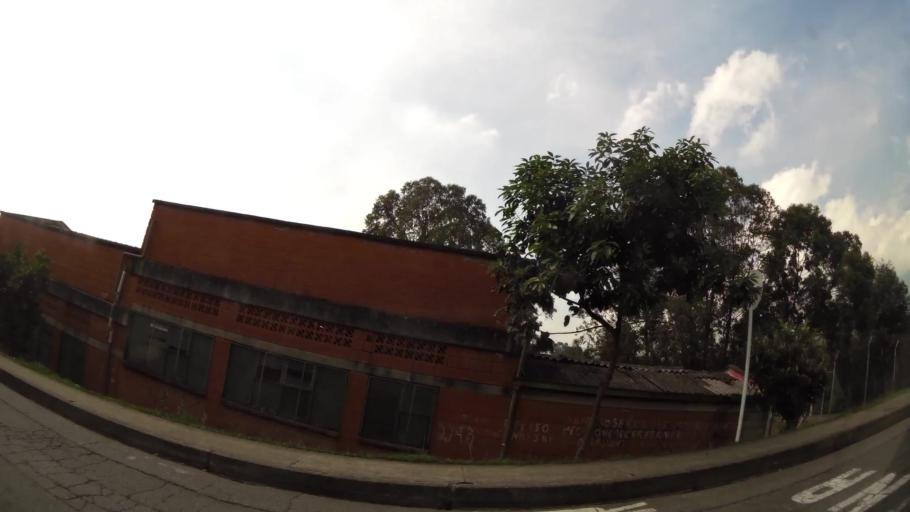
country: CO
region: Antioquia
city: La Estrella
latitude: 6.1747
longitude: -75.6423
